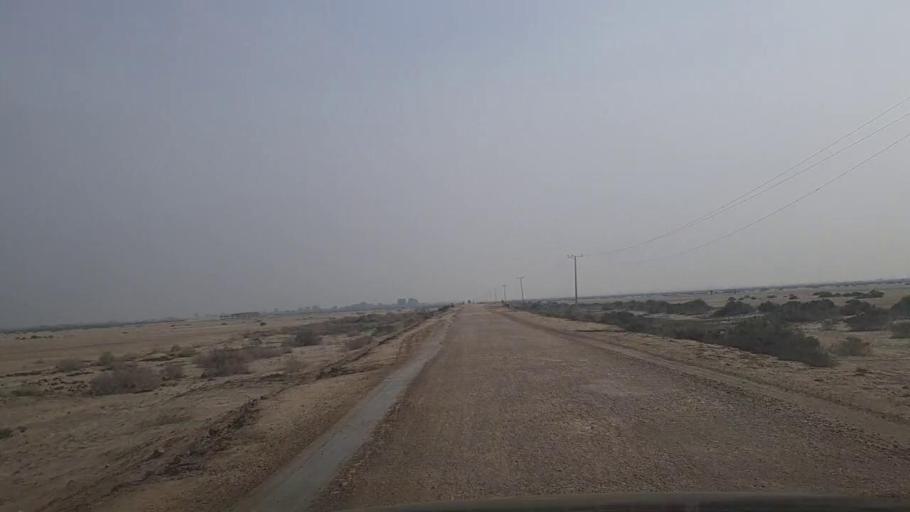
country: PK
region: Sindh
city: Mirpur Sakro
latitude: 24.4647
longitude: 67.6865
